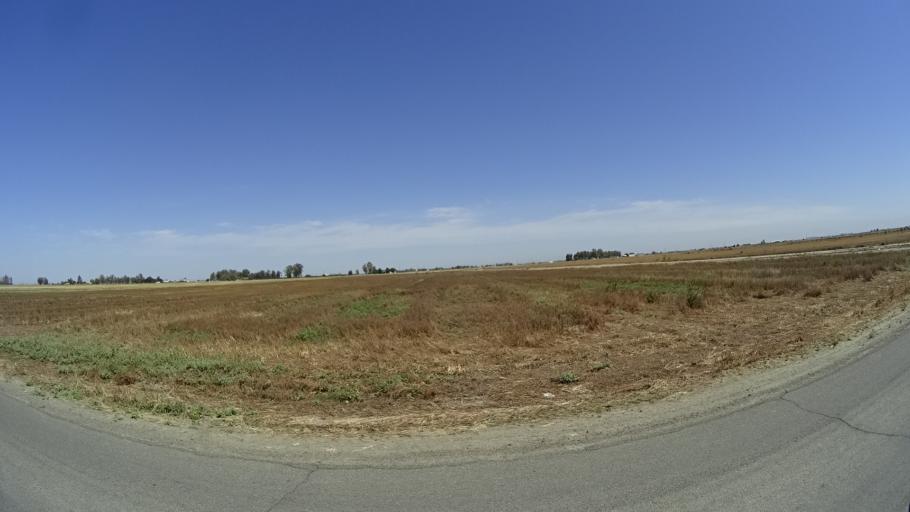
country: US
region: California
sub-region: Kings County
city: Stratford
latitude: 36.1890
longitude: -119.7838
